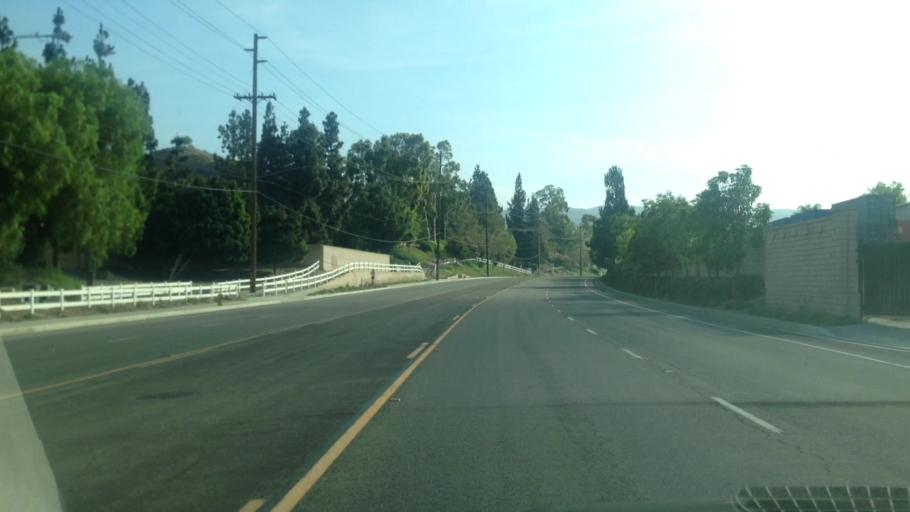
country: US
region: California
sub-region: Orange County
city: Yorba Linda
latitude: 33.8702
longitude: -117.7735
